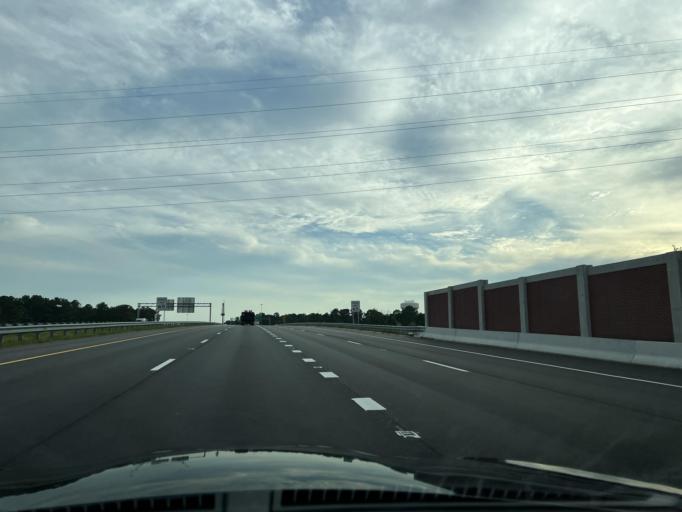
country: US
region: North Carolina
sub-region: Durham County
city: Durham
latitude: 35.9708
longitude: -78.8593
